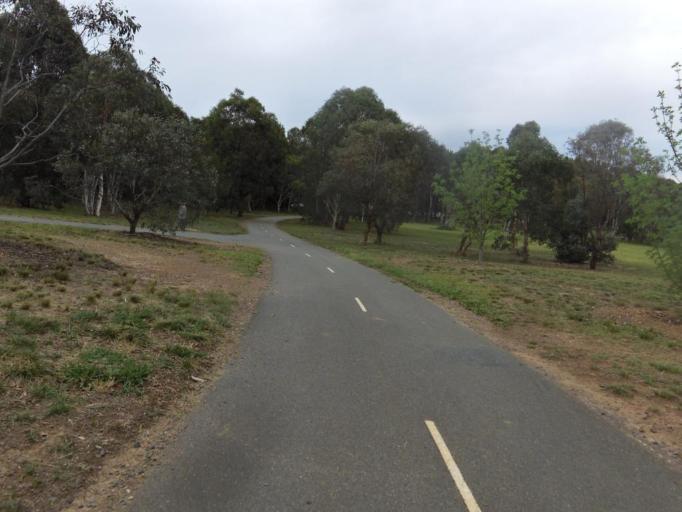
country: AU
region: Australian Capital Territory
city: Kaleen
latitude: -35.1807
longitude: 149.1288
